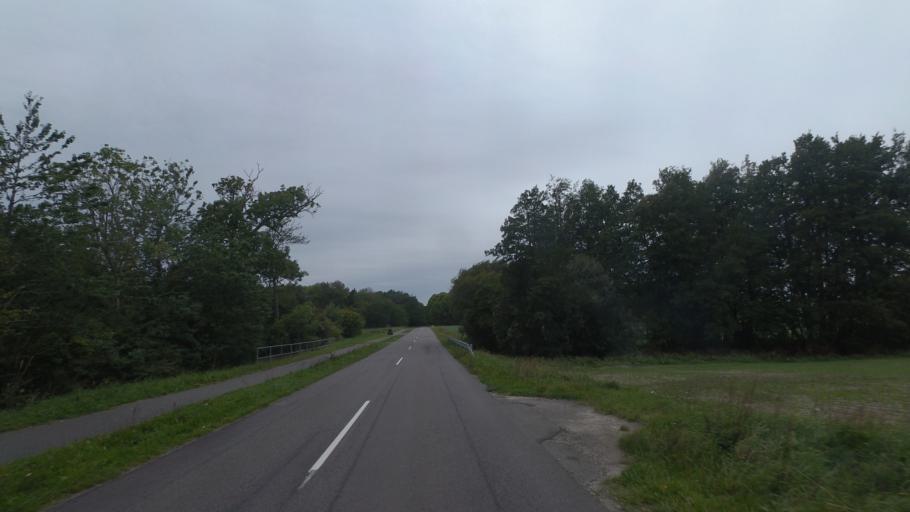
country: DK
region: Capital Region
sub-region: Bornholm Kommune
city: Nexo
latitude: 55.0022
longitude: 15.0494
